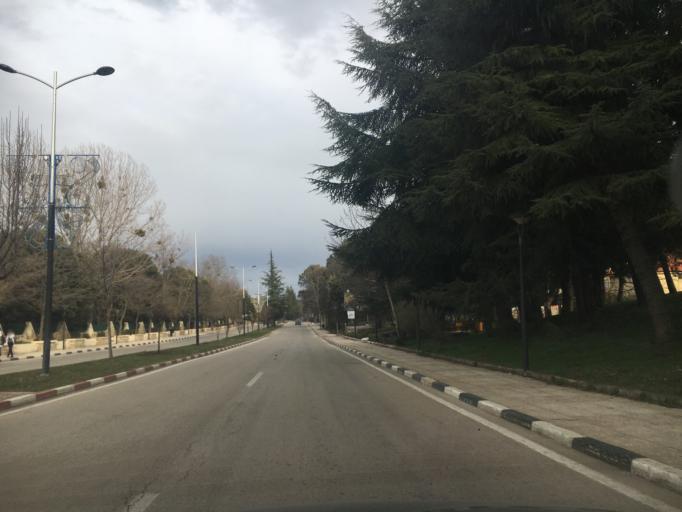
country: MA
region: Meknes-Tafilalet
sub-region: Ifrane
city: Ifrane
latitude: 33.5275
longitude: -5.1207
